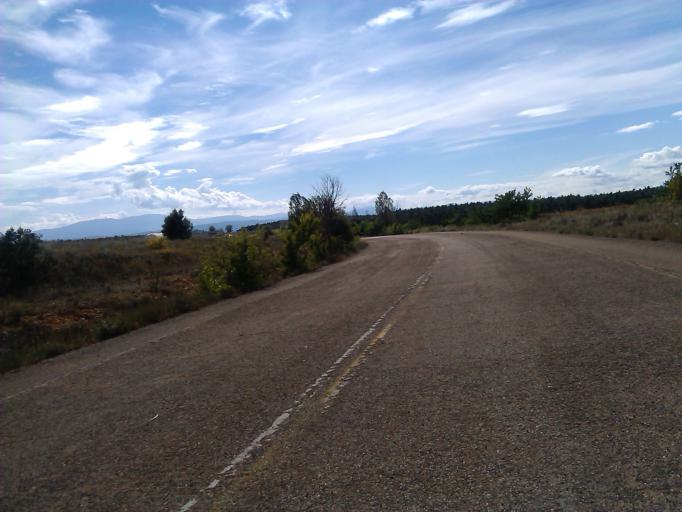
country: ES
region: Castille and Leon
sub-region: Provincia de Leon
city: San Justo de la Vega
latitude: 42.4535
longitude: -5.9901
